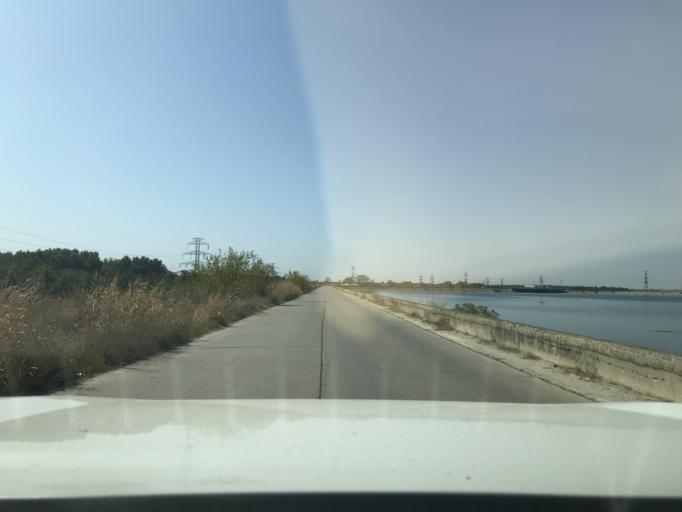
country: RO
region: Olt
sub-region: Municipiul Slatina
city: Slatina
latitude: 44.3994
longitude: 24.3541
